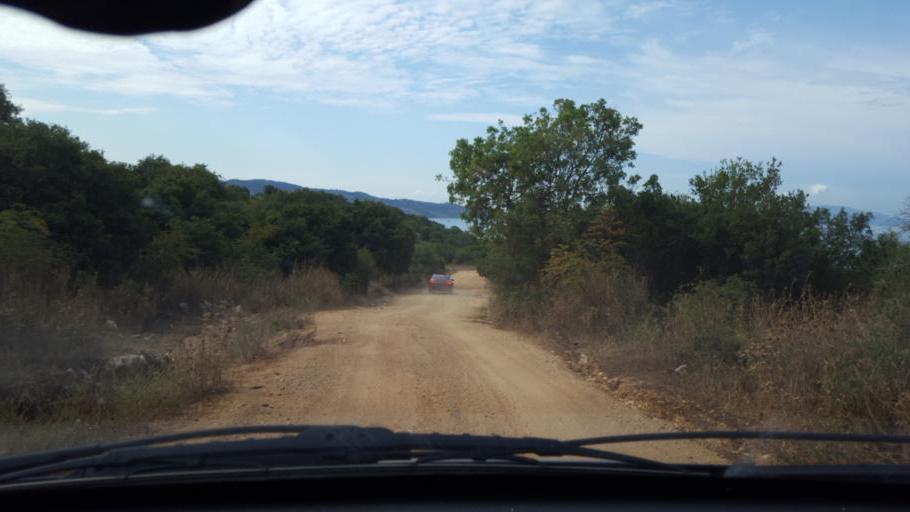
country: AL
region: Vlore
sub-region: Rrethi i Sarandes
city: Xarre
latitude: 39.7507
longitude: 19.9772
